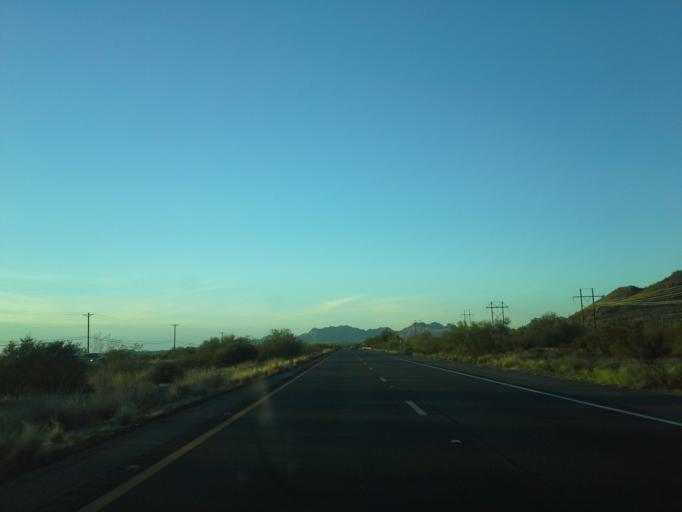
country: US
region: Arizona
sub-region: Pinal County
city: Apache Junction
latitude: 33.3704
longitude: -111.4814
